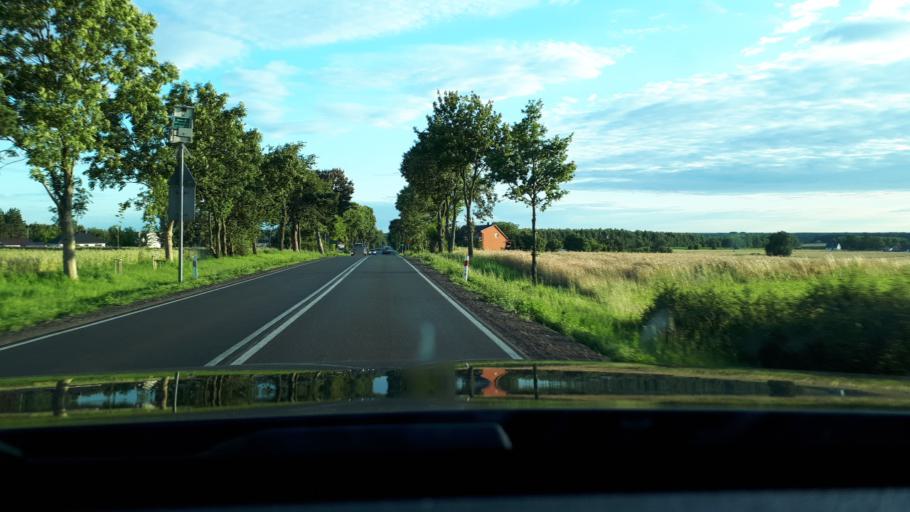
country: PL
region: Masovian Voivodeship
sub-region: Powiat ciechanowski
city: Ojrzen
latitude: 52.7764
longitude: 20.5528
